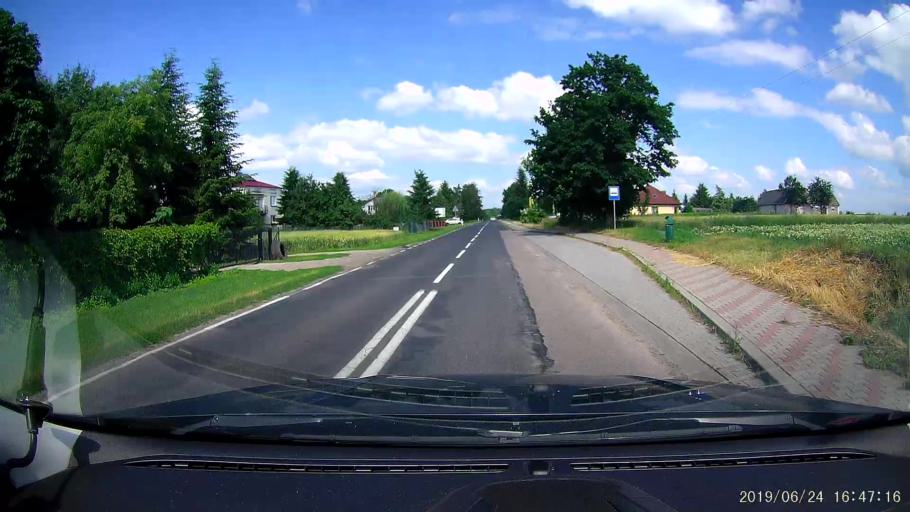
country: PL
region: Lublin Voivodeship
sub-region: Powiat tomaszowski
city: Laszczow
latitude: 50.5298
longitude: 23.6970
